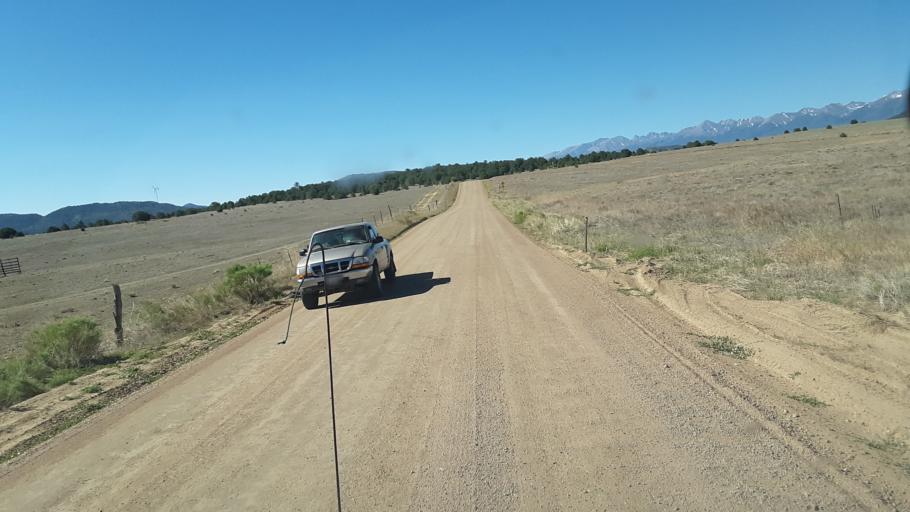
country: US
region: Colorado
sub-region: Custer County
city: Westcliffe
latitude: 38.2873
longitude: -105.4911
